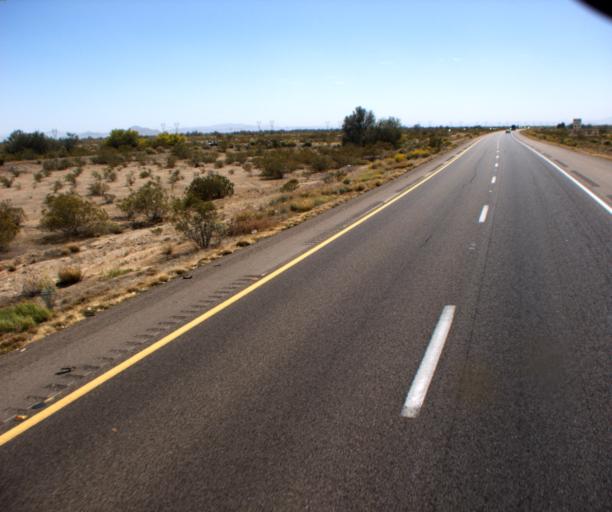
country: US
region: Arizona
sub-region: Maricopa County
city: Gila Bend
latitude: 33.0416
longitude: -112.6456
